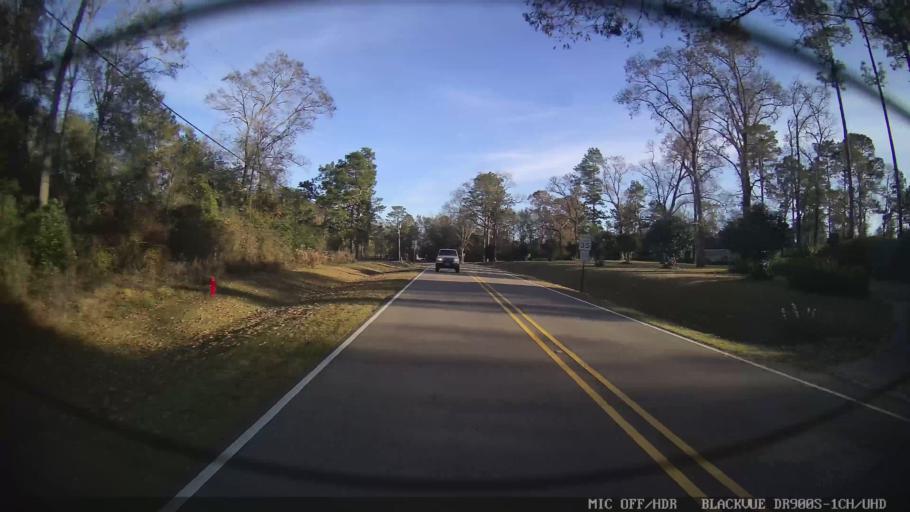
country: US
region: Mississippi
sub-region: Lamar County
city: Purvis
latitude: 31.1386
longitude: -89.3657
